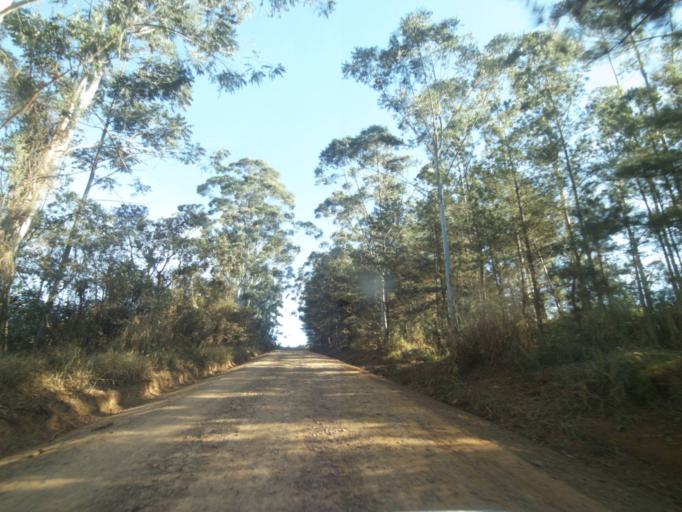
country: BR
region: Parana
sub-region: Tibagi
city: Tibagi
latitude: -24.5250
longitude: -50.5074
